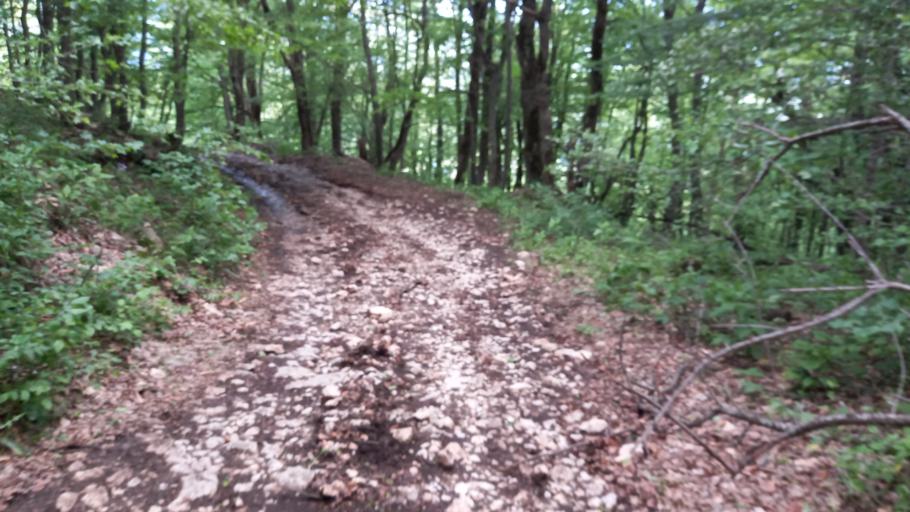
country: RU
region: Adygeya
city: Kamennomostskiy
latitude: 44.2223
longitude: 40.0017
